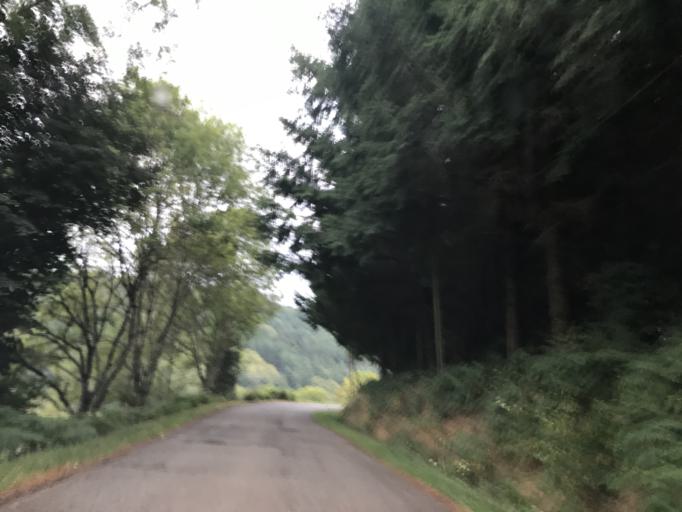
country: FR
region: Auvergne
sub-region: Departement du Puy-de-Dome
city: Thiers
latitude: 45.8514
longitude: 3.5821
